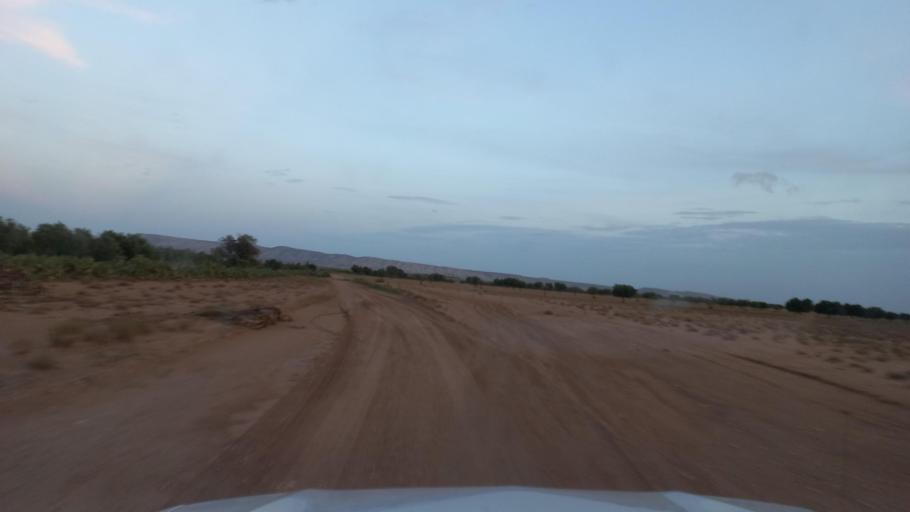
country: TN
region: Al Qasrayn
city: Sbiba
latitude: 35.3491
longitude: 9.0459
